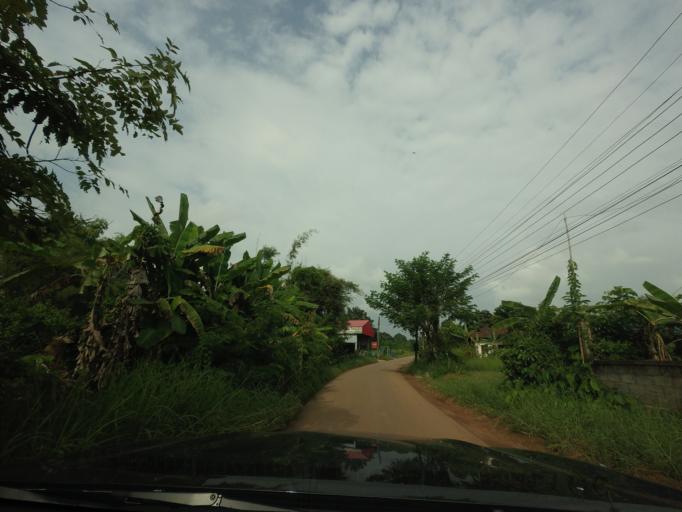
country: TH
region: Nong Khai
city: Nong Khai
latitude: 17.8152
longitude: 102.7205
